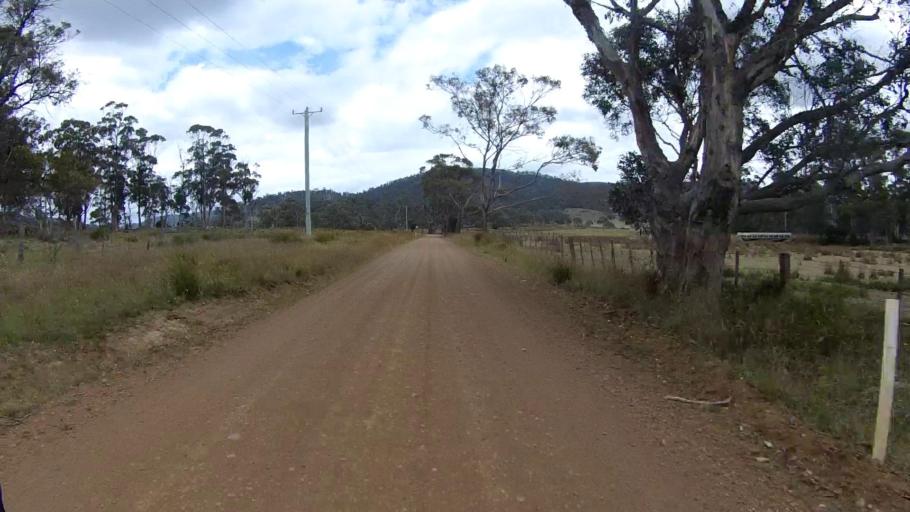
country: AU
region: Tasmania
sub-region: Sorell
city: Sorell
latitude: -42.6431
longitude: 147.9026
